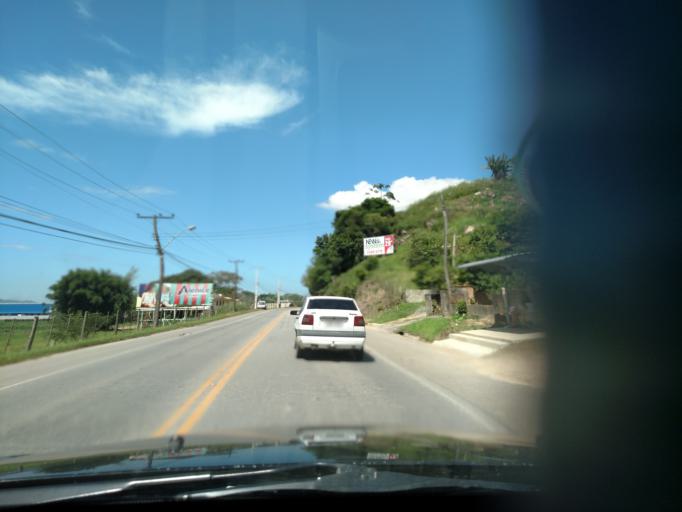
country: BR
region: Santa Catarina
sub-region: Itajai
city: Itajai
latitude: -26.8861
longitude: -48.7423
